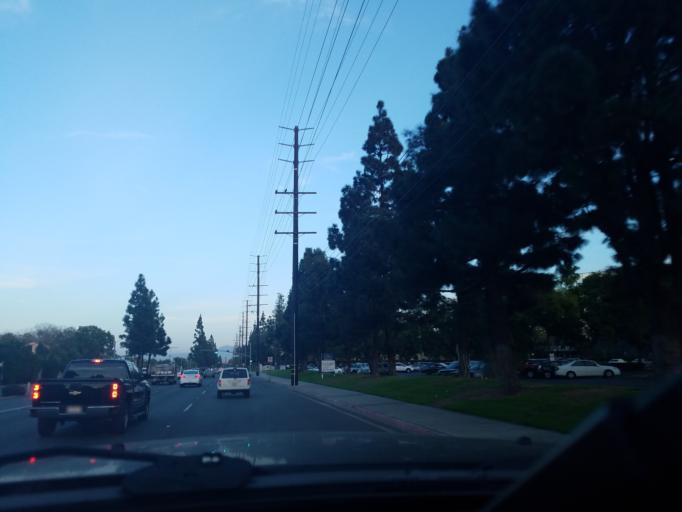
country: US
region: California
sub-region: Orange County
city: Fountain Valley
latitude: 33.7163
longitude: -117.9345
